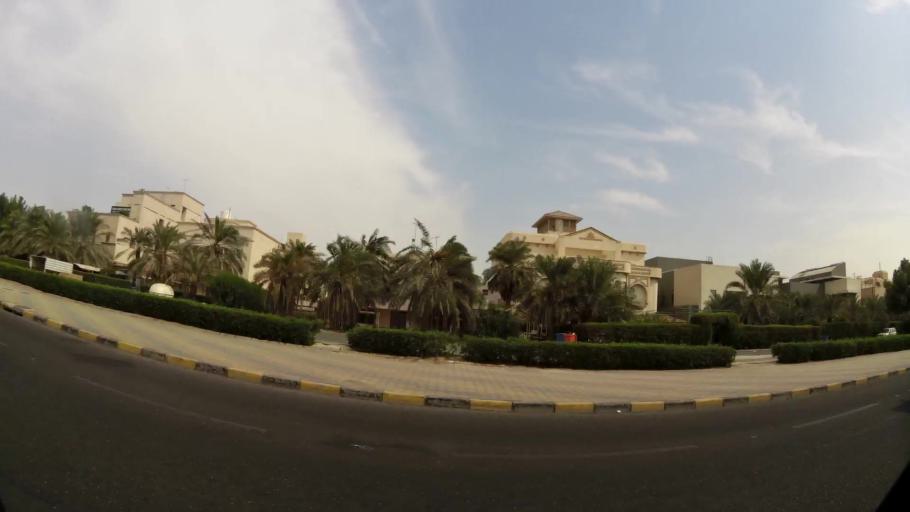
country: KW
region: Al Asimah
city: Ash Shamiyah
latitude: 29.3337
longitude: 47.9880
